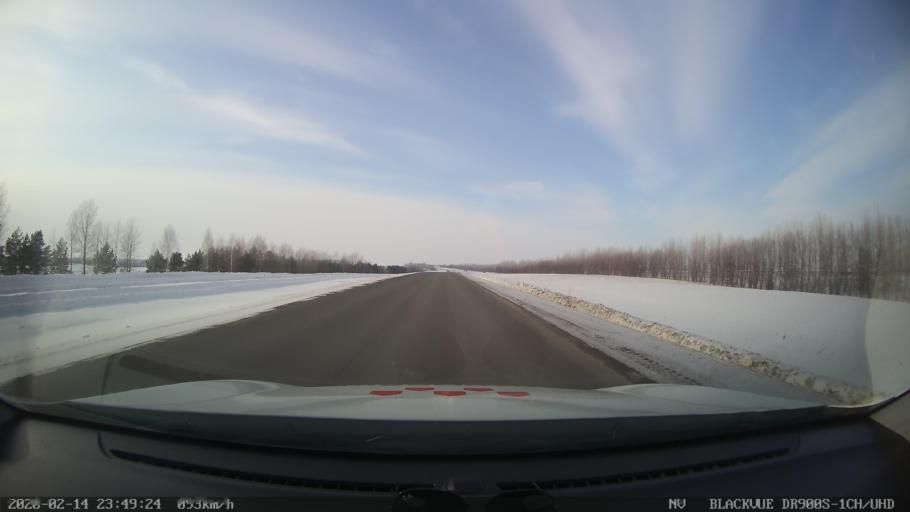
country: RU
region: Tatarstan
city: Kuybyshevskiy Zaton
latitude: 55.2535
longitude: 49.1827
